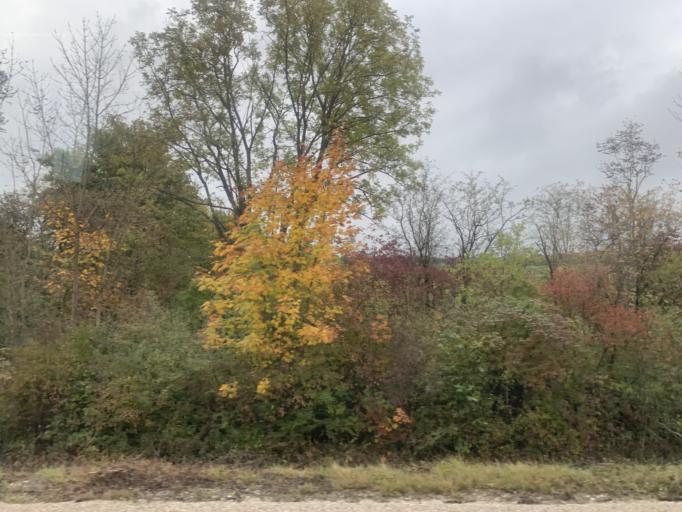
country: DE
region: Bavaria
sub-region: Upper Bavaria
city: Unterschleissheim
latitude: 48.2918
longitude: 11.5878
